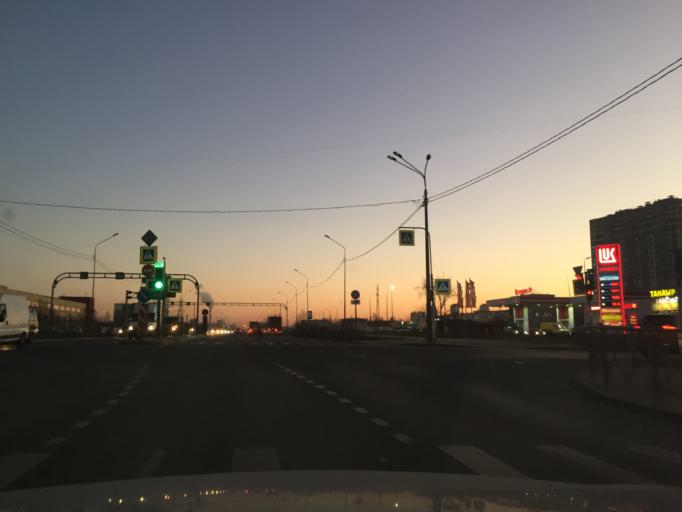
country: RU
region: St.-Petersburg
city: Obukhovo
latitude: 59.8639
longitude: 30.4169
